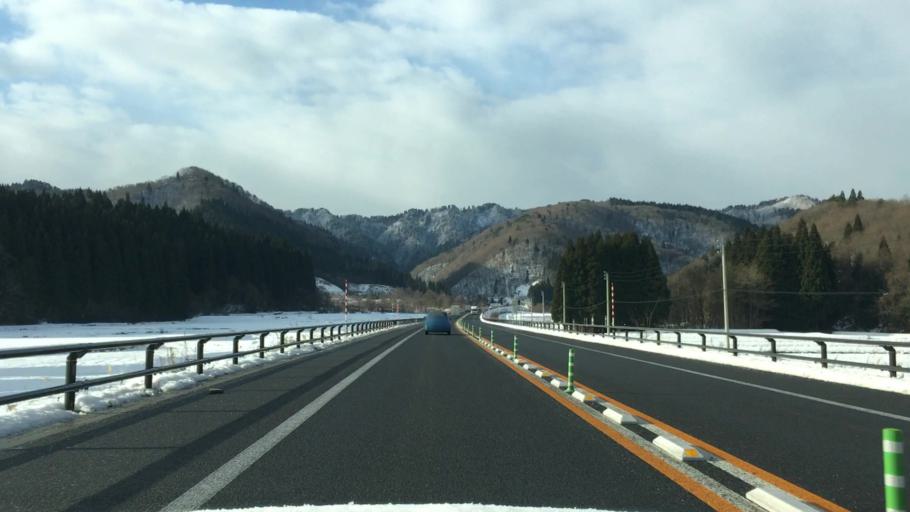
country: JP
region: Akita
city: Odate
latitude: 40.2353
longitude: 140.4989
